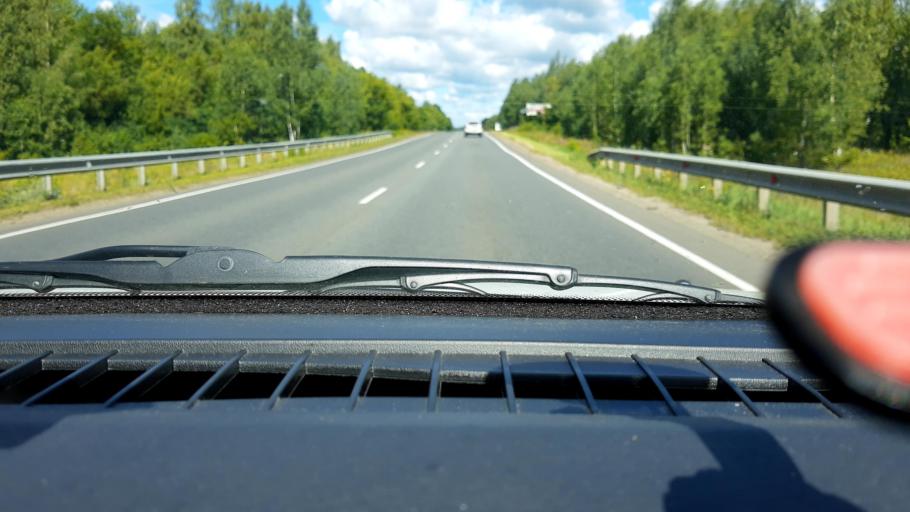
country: RU
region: Nizjnij Novgorod
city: Arzamas
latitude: 55.2853
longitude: 43.9500
